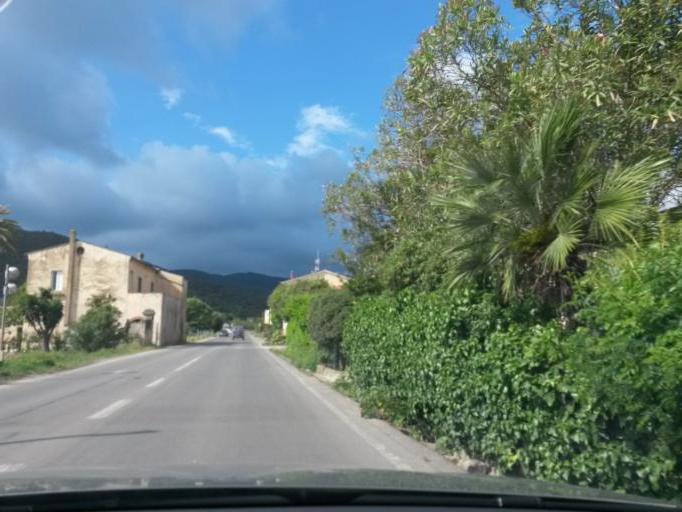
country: IT
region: Tuscany
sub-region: Provincia di Livorno
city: Portoferraio
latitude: 42.7998
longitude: 10.3052
